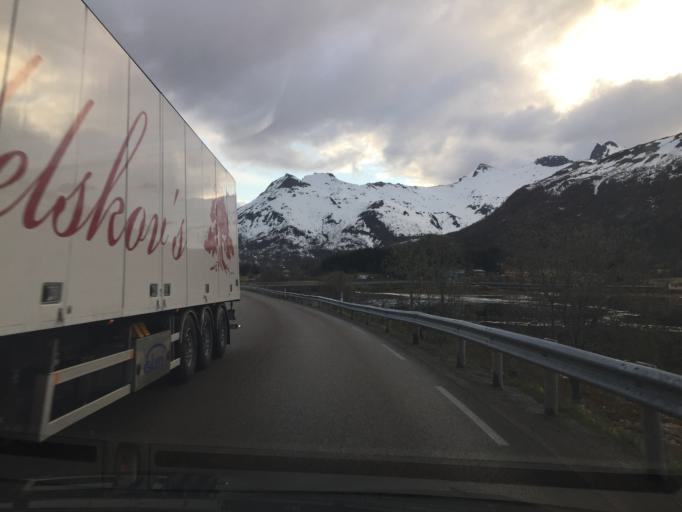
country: NO
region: Nordland
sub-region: Vagan
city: Svolvaer
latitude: 68.3244
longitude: 14.6959
